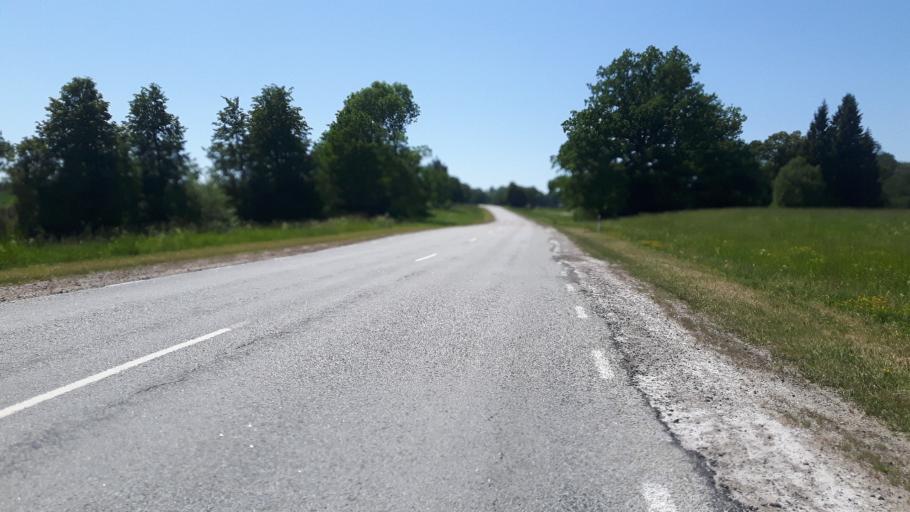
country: EE
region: Paernumaa
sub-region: Sindi linn
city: Sindi
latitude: 58.4420
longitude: 24.7509
